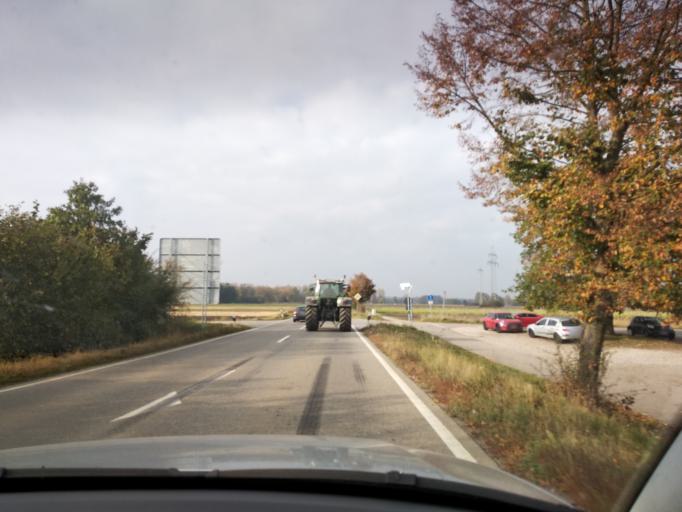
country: DE
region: Bavaria
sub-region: Upper Bavaria
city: Forstinning
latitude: 48.1728
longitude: 11.8881
